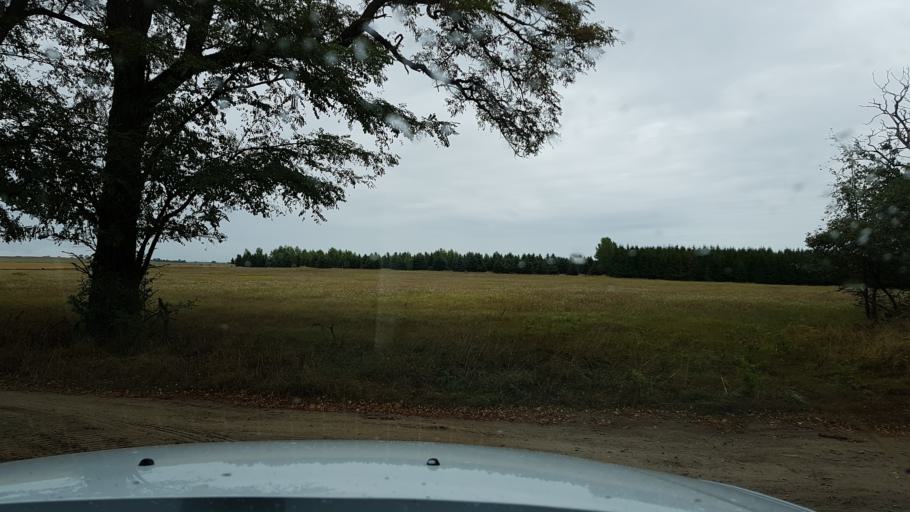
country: PL
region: West Pomeranian Voivodeship
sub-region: Powiat gryfinski
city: Moryn
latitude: 52.8368
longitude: 14.3005
